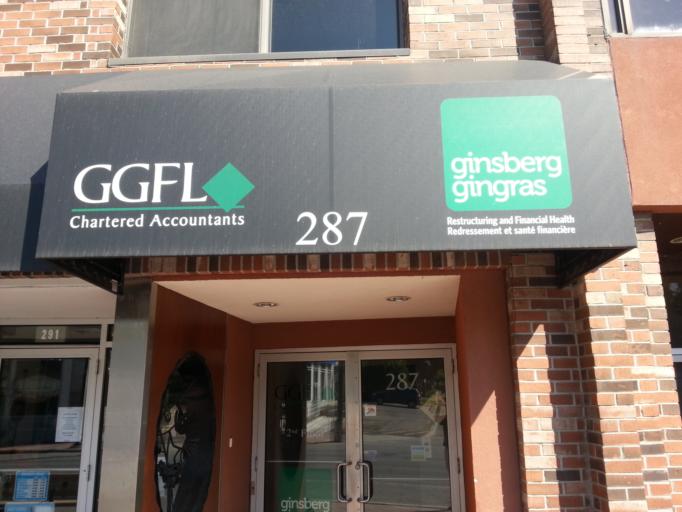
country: CA
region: Ontario
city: Ottawa
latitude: 45.3932
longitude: -75.7516
